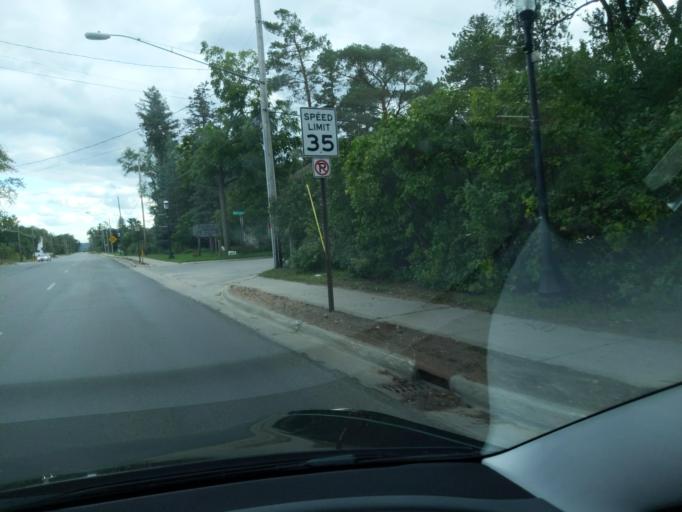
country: US
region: Michigan
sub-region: Kalkaska County
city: Rapid City
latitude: 44.8327
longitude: -85.2828
